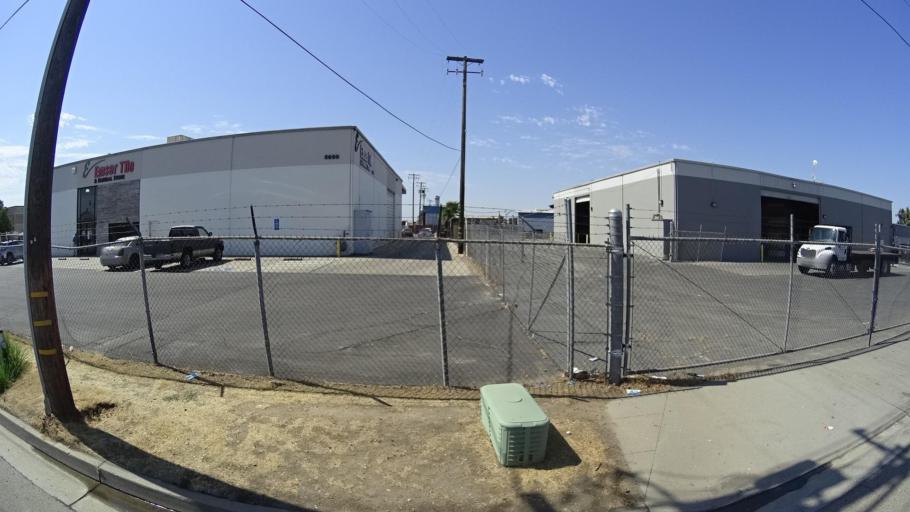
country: US
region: California
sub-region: Fresno County
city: Tarpey Village
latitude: 36.7721
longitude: -119.6991
